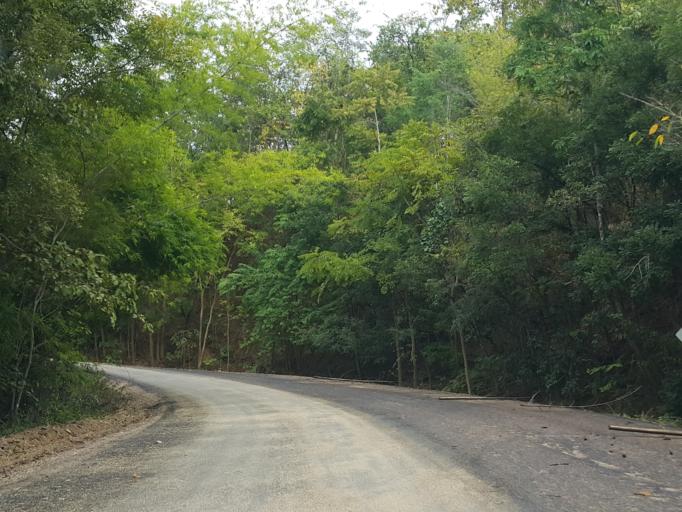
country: TH
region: Lampang
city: Chae Hom
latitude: 18.6484
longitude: 99.5029
